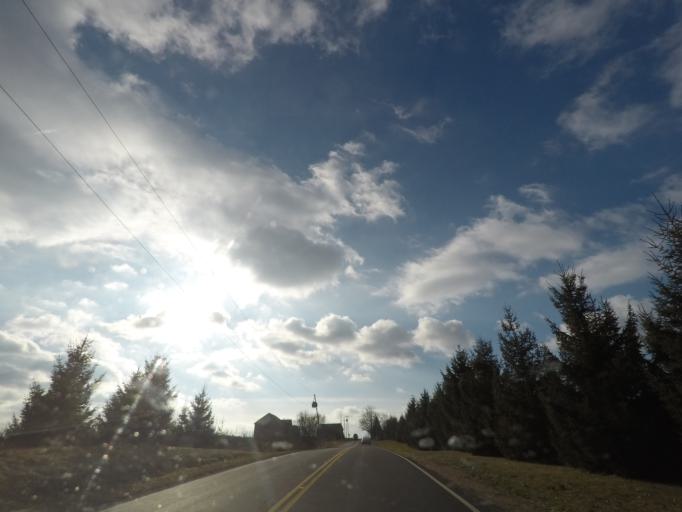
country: US
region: New York
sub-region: Albany County
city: Voorheesville
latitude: 42.6602
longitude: -73.8950
